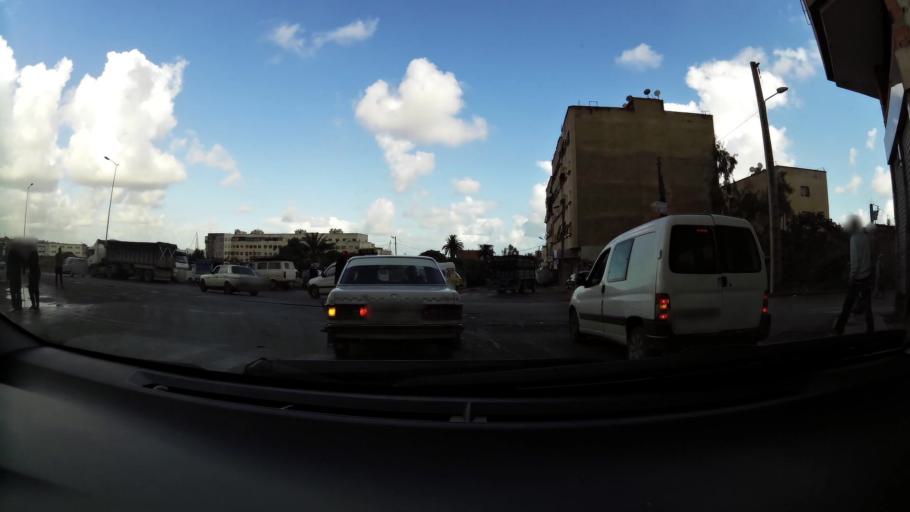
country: MA
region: Grand Casablanca
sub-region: Mediouna
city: Tit Mellil
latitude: 33.5828
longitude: -7.5369
